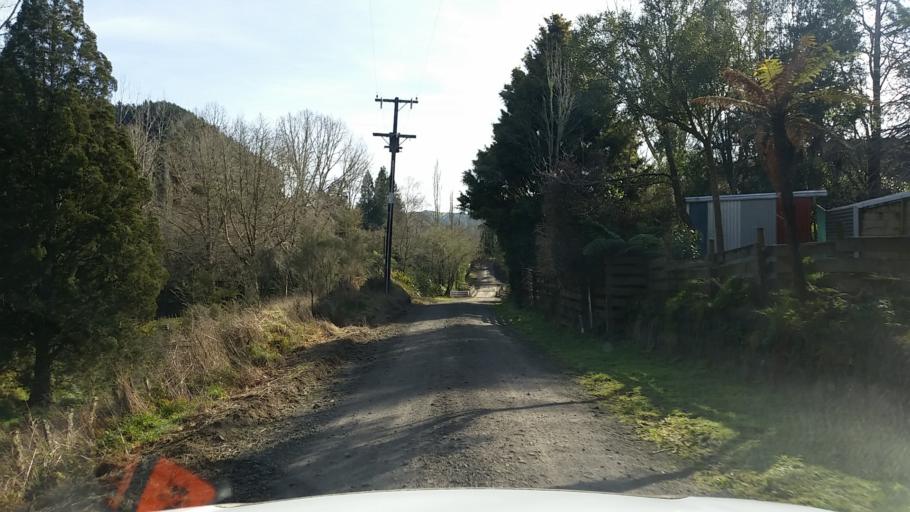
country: NZ
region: Taranaki
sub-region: South Taranaki District
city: Eltham
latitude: -39.3602
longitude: 174.5131
